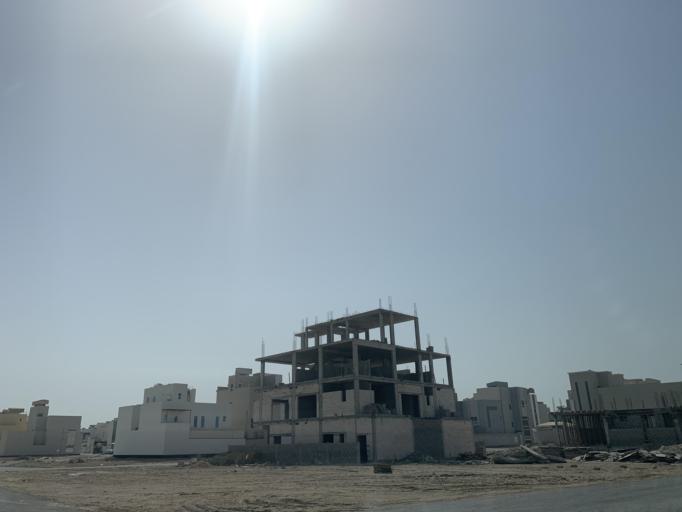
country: BH
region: Manama
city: Jidd Hafs
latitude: 26.2094
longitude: 50.5138
